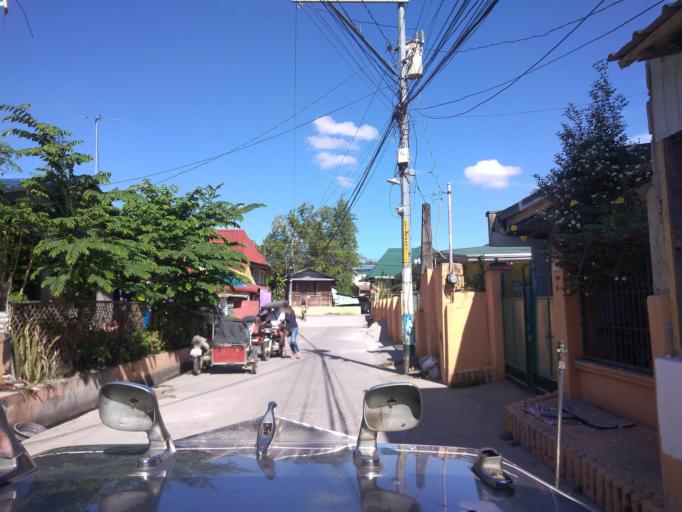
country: PH
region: Central Luzon
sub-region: Province of Pampanga
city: Santa Rita
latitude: 14.9934
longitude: 120.6114
